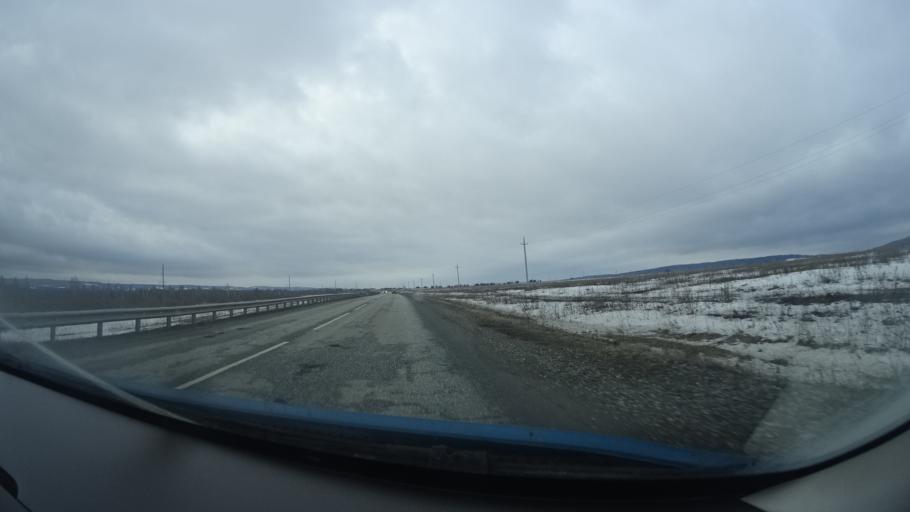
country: RU
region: Perm
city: Barda
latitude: 56.9612
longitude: 55.5793
